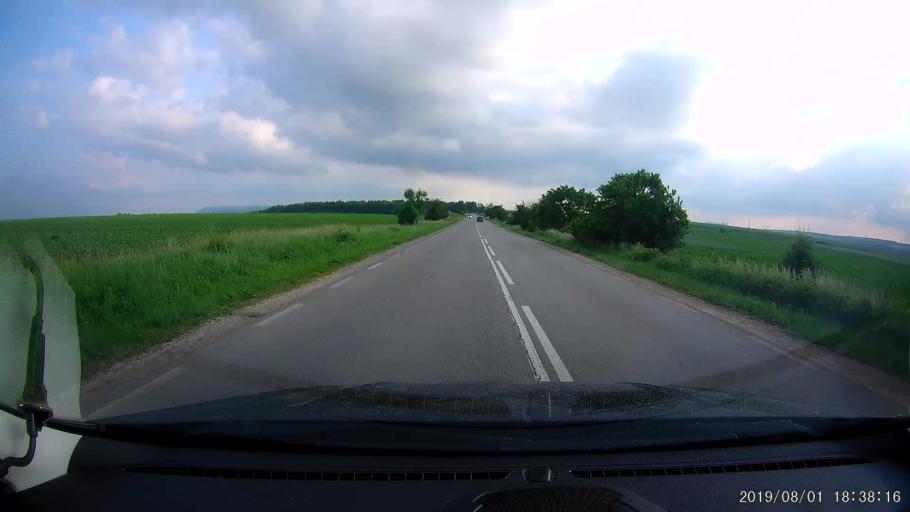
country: BG
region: Shumen
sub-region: Obshtina Khitrino
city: Gara Khitrino
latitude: 43.4049
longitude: 26.9189
